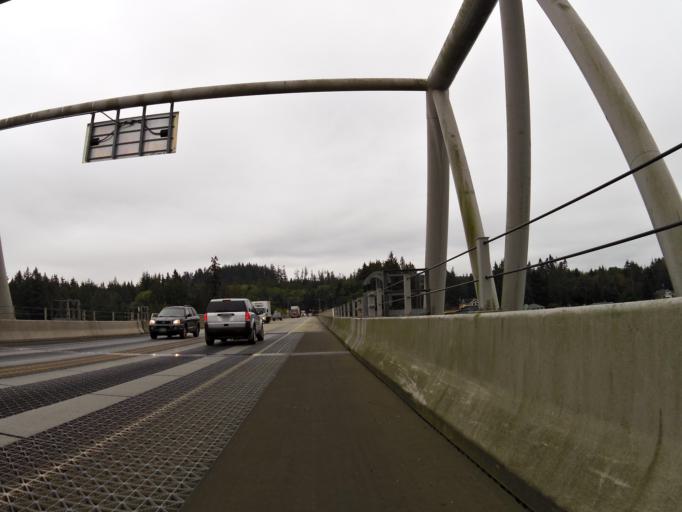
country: US
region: Washington
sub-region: Kitsap County
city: Lofall
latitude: 47.8539
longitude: -122.6140
